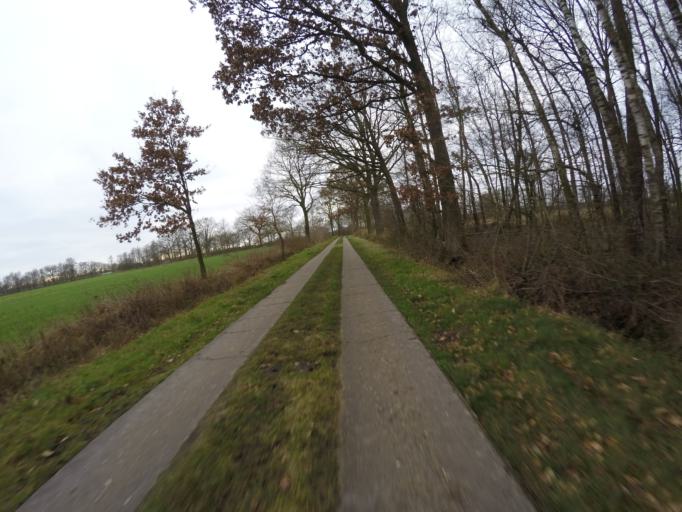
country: DE
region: Schleswig-Holstein
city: Hemdingen
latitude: 53.7837
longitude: 9.8381
